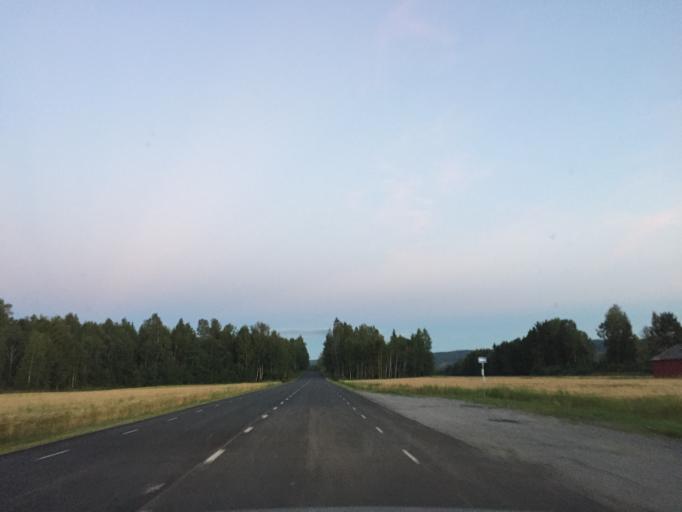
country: NO
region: Hedmark
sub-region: Kongsvinger
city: Spetalen
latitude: 60.2246
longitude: 11.8562
